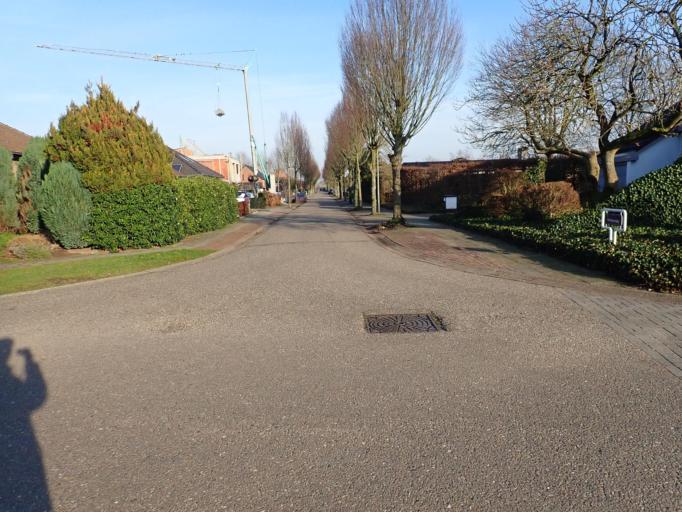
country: BE
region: Flanders
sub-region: Provincie Antwerpen
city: Essen
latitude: 51.4503
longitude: 4.4481
